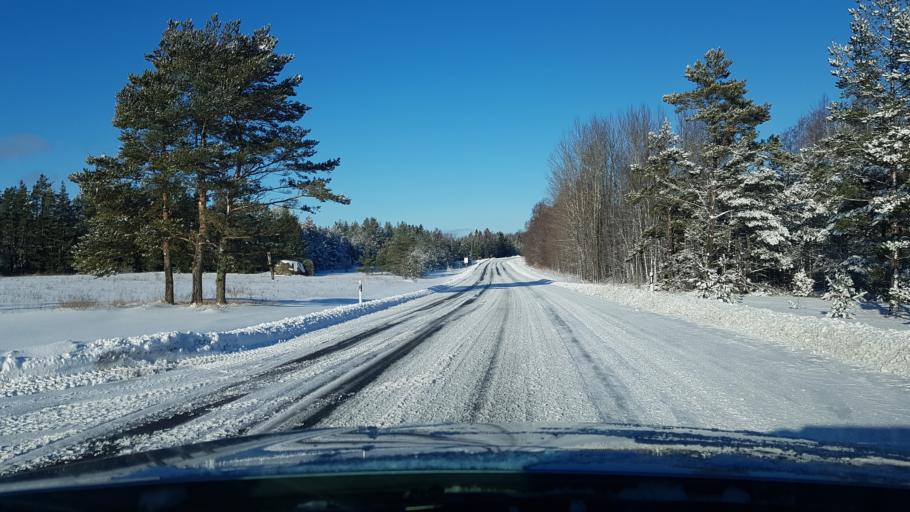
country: EE
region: Hiiumaa
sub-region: Kaerdla linn
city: Kardla
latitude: 58.9590
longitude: 22.7731
